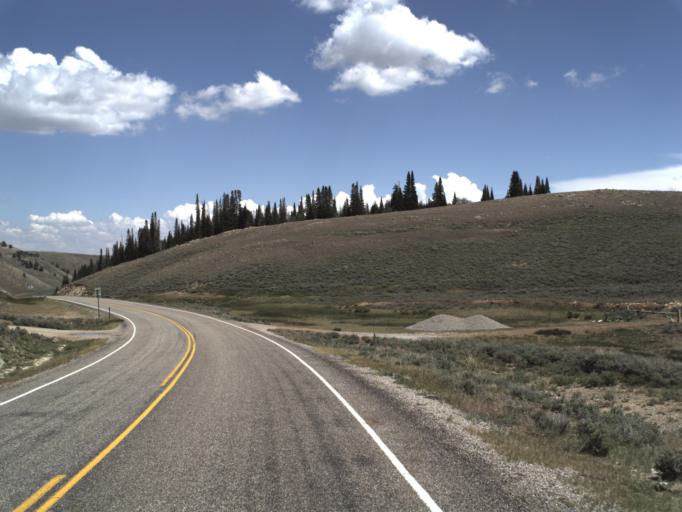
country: US
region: Utah
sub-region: Rich County
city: Randolph
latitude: 41.4837
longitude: -111.4214
